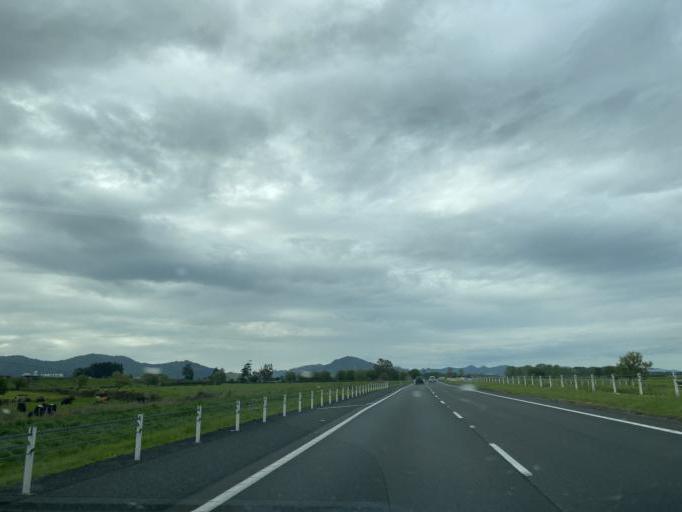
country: NZ
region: Waikato
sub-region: Waikato District
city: Ngaruawahia
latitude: -37.6624
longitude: 175.2062
